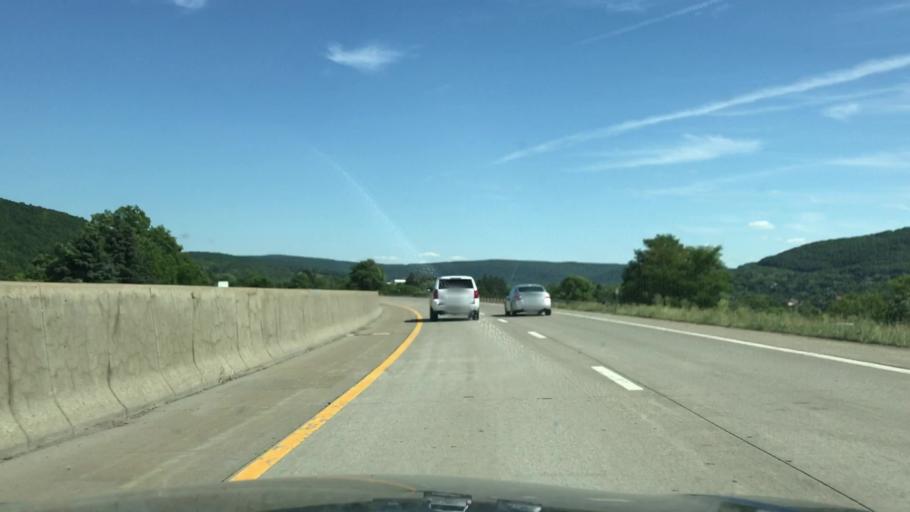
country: US
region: New York
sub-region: Steuben County
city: Corning
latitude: 42.1564
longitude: -77.0550
